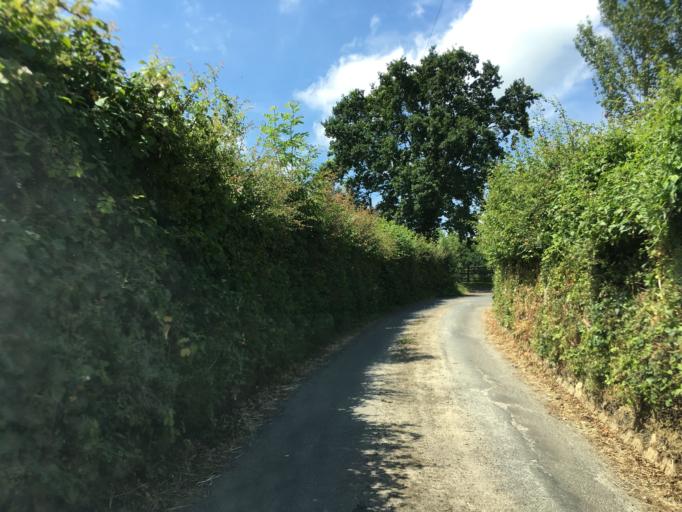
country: GB
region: Wales
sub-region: Newport
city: Llanwern
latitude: 51.5934
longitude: -2.9127
